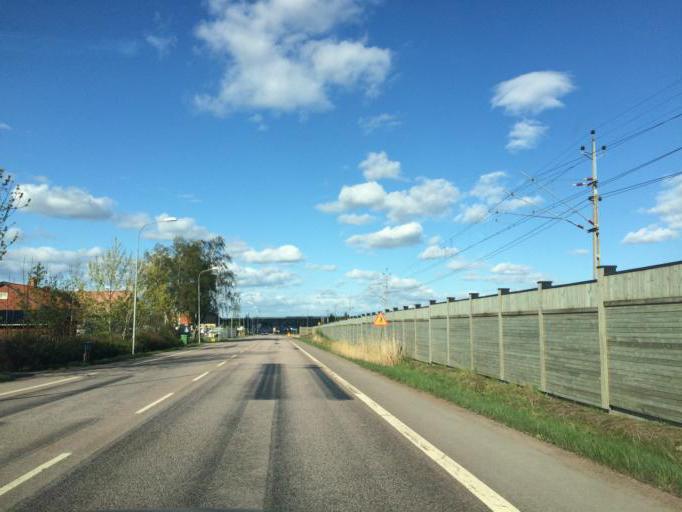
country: SE
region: Vaestmanland
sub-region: Hallstahammars Kommun
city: Kolback
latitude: 59.5580
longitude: 16.2181
